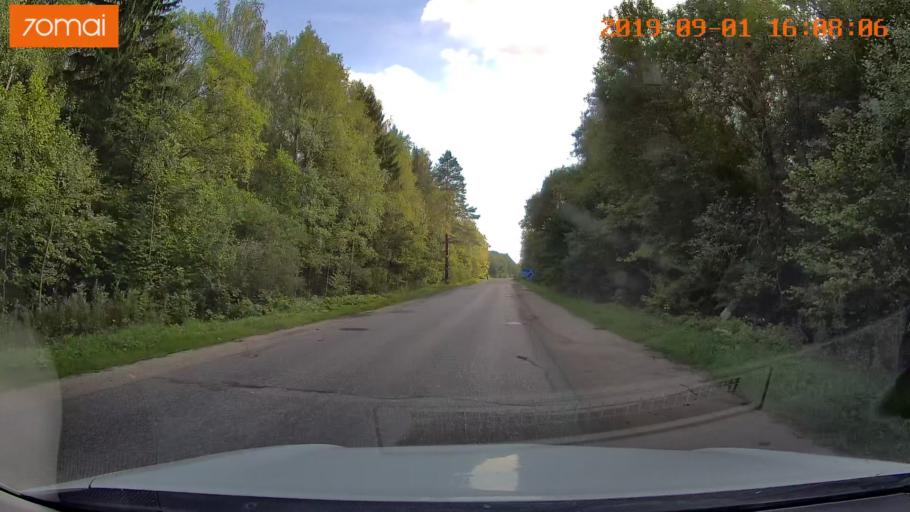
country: RU
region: Kaluga
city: Maloyaroslavets
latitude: 54.9833
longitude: 36.4710
